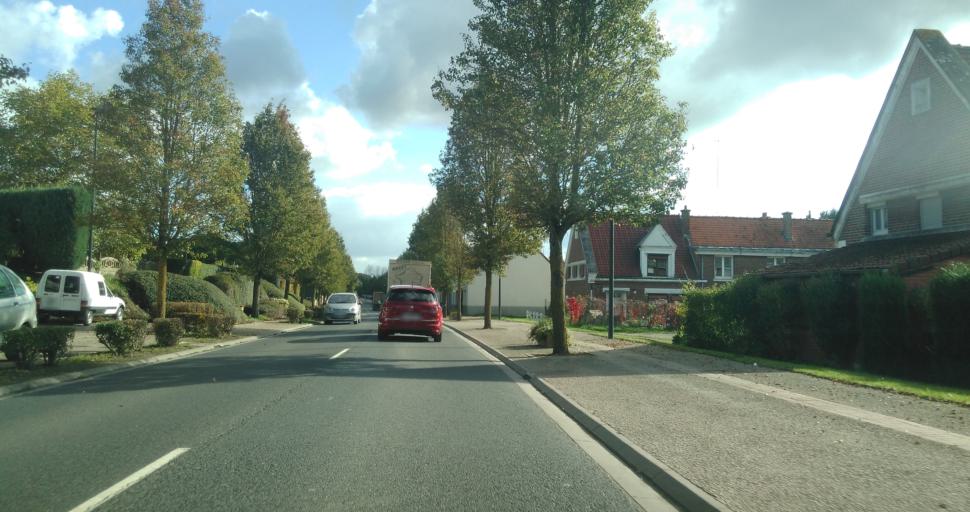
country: FR
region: Picardie
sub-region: Departement de la Somme
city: Doullens
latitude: 50.1618
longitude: 2.3301
